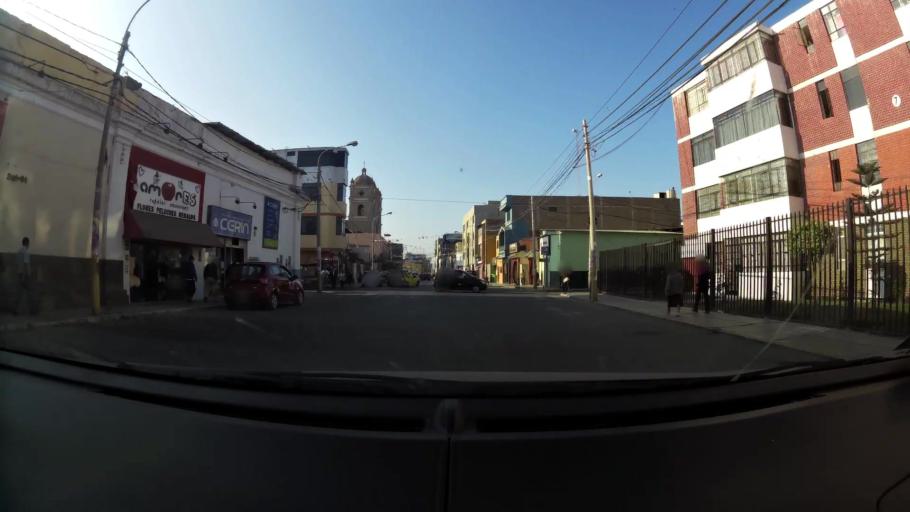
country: PE
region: Lambayeque
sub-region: Provincia de Chiclayo
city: Chiclayo
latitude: -6.7751
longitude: -79.8426
